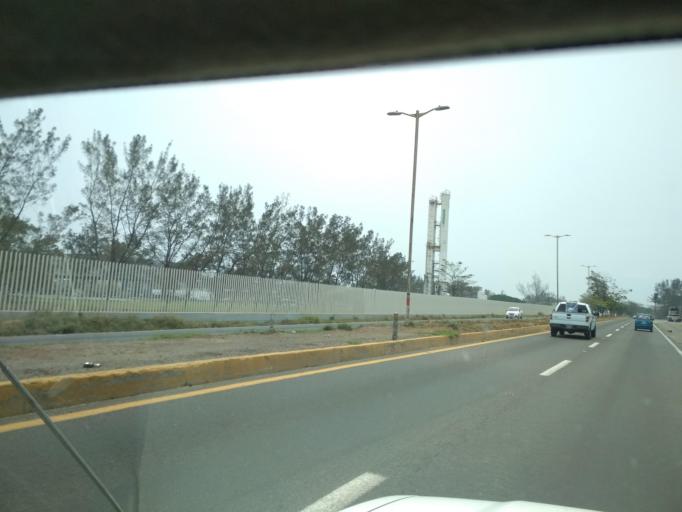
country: MX
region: Veracruz
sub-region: Veracruz
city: Oasis
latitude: 19.1748
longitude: -96.2378
